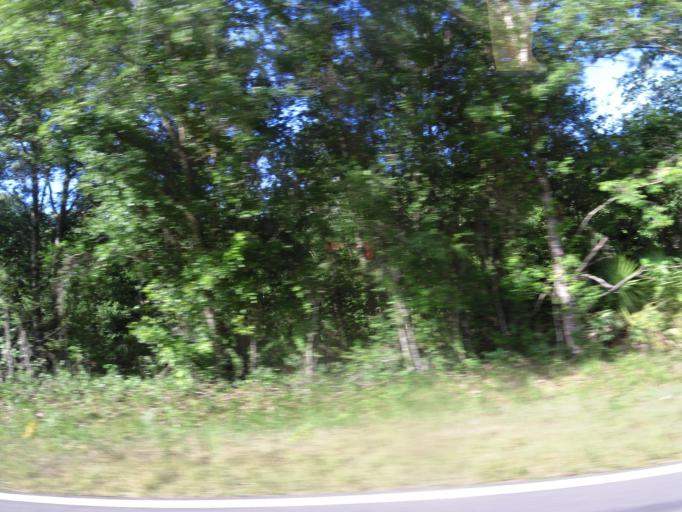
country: US
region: Florida
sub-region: Nassau County
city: Nassau Village-Ratliff
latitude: 30.4812
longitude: -81.8456
